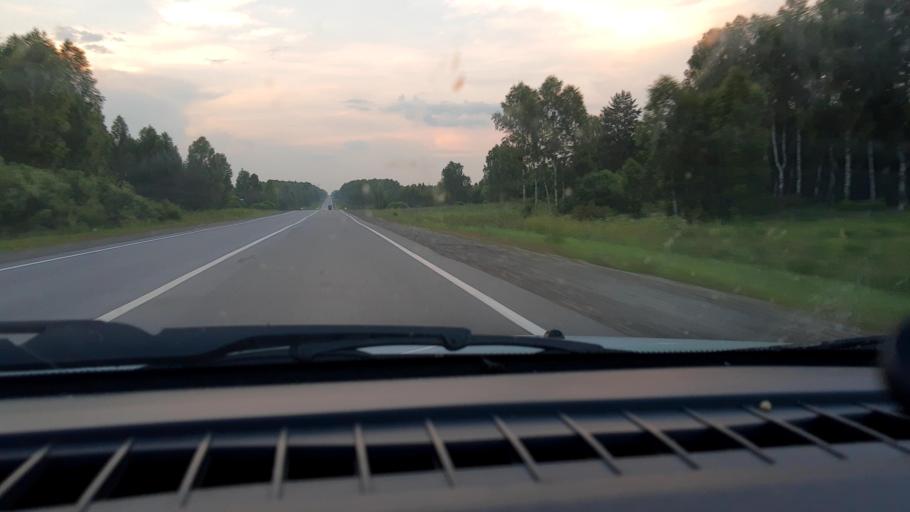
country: RU
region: Nizjnij Novgorod
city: Arzamas
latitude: 55.5470
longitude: 43.9387
